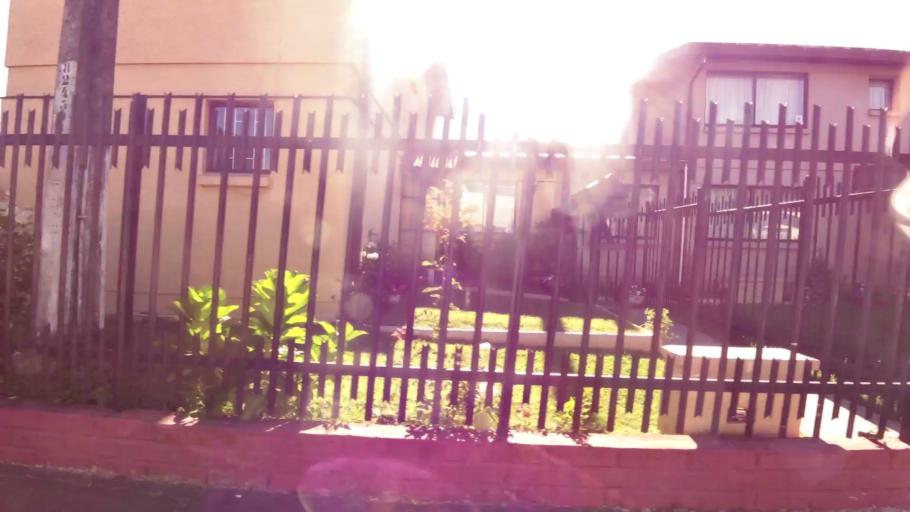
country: CL
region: Biobio
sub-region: Provincia de Concepcion
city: Concepcion
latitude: -36.8415
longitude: -73.1050
